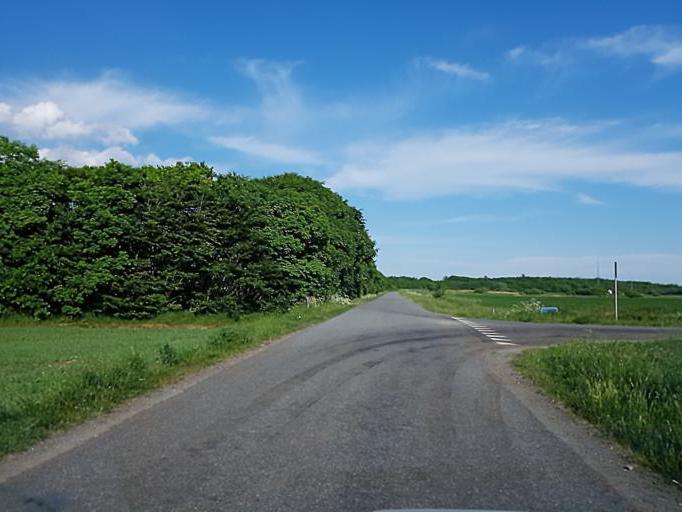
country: DK
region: South Denmark
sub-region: Esbjerg Kommune
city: Esbjerg
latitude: 55.5415
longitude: 8.4285
